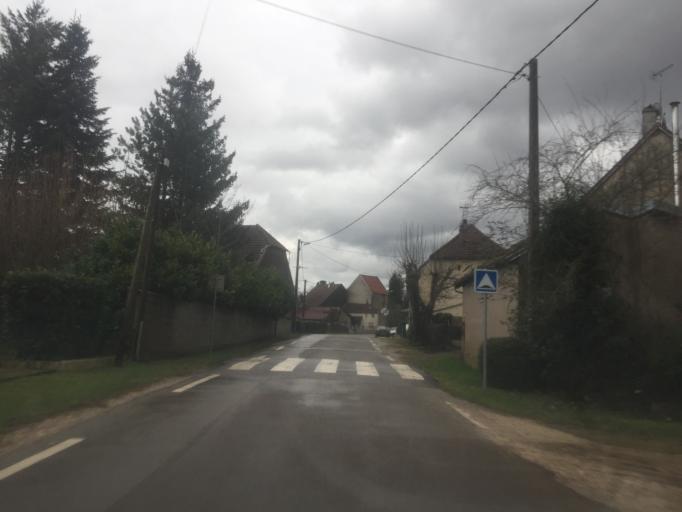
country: FR
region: Franche-Comte
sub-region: Departement de la Haute-Saone
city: Pesmes
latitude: 47.2176
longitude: 5.5160
